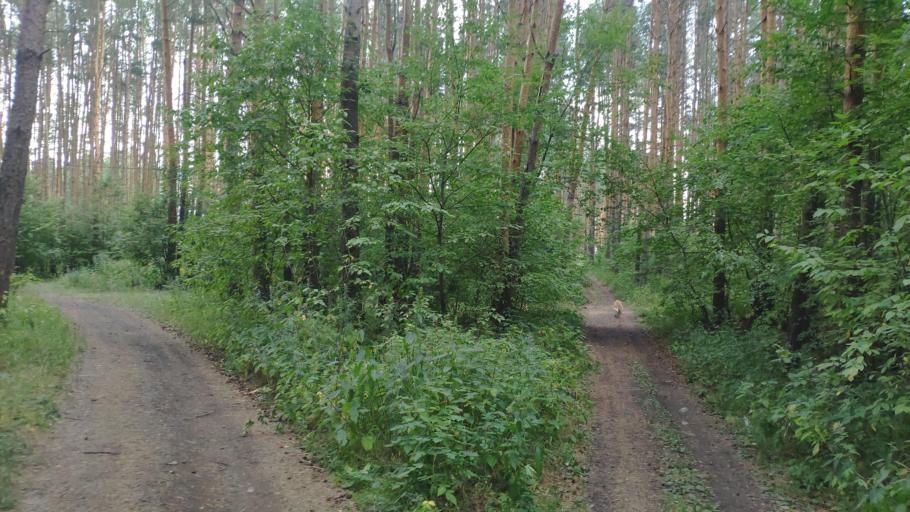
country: RU
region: Bashkortostan
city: Abzakovo
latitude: 53.8096
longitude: 58.6393
